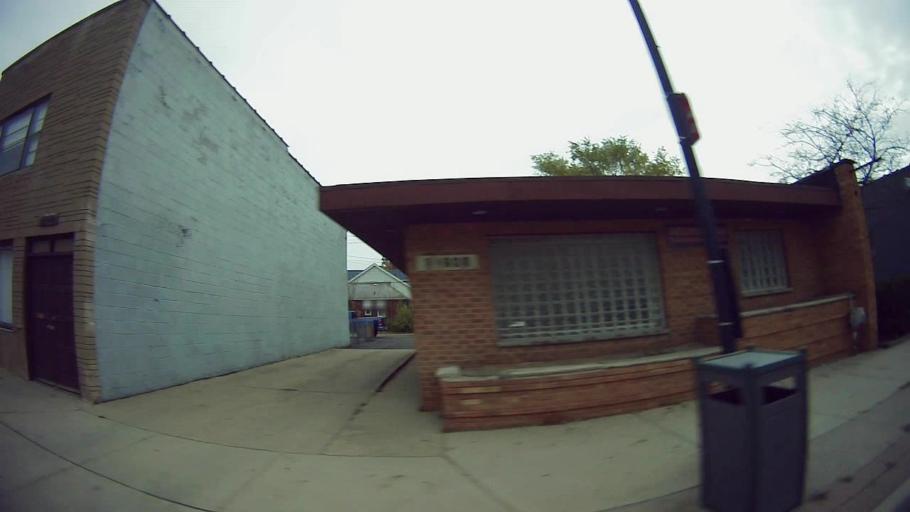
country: US
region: Michigan
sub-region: Oakland County
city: Hazel Park
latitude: 42.4566
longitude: -83.1035
